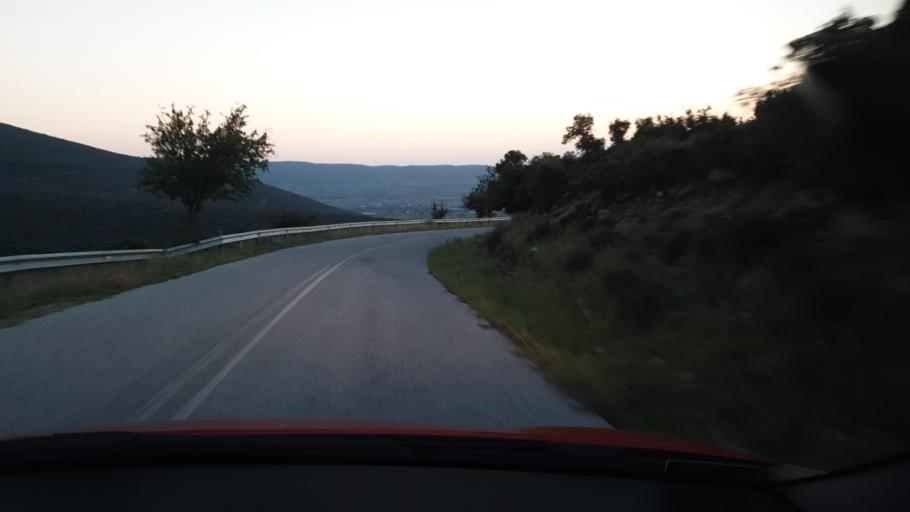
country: GR
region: Central Macedonia
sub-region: Nomos Thessalonikis
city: Peristera
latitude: 40.5120
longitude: 23.1682
